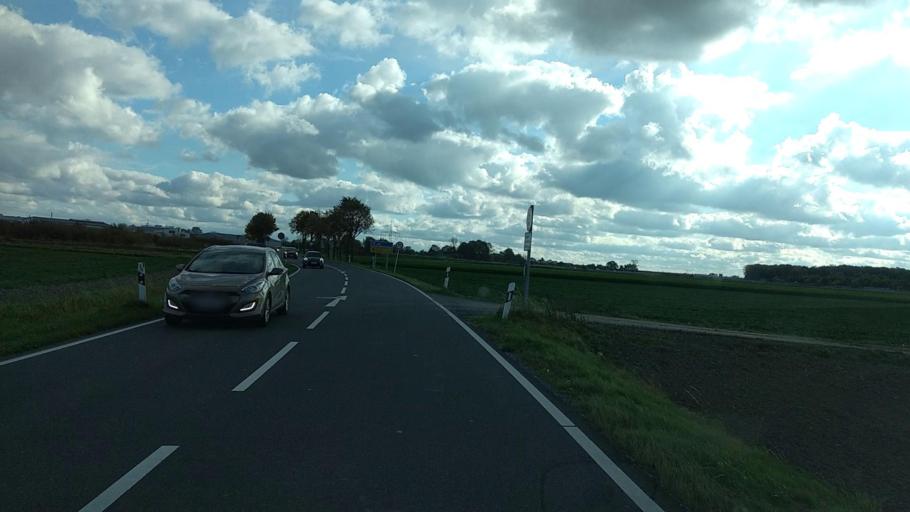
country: DE
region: North Rhine-Westphalia
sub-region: Regierungsbezirk Koln
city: Bergheim
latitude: 50.9004
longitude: 6.6410
